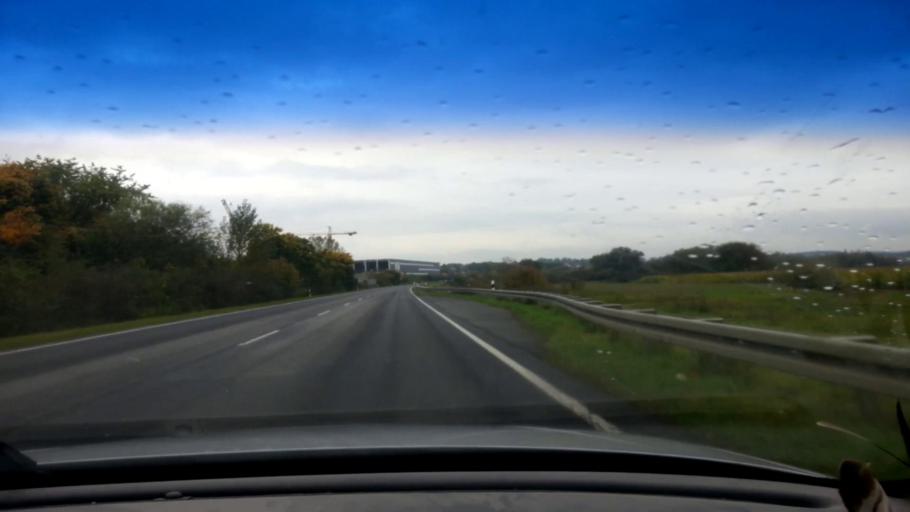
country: DE
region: Bavaria
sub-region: Upper Franconia
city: Bischberg
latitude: 49.9131
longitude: 10.8543
